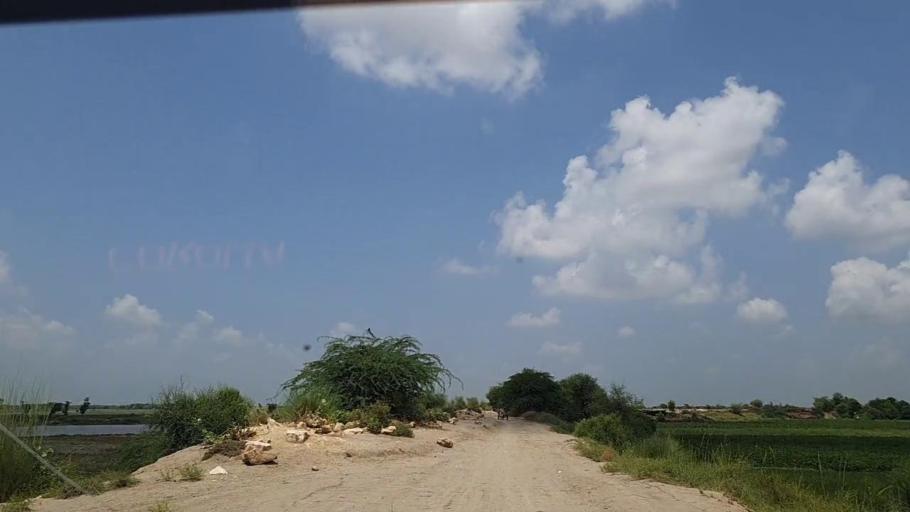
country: PK
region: Sindh
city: Tharu Shah
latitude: 26.9665
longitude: 68.0313
